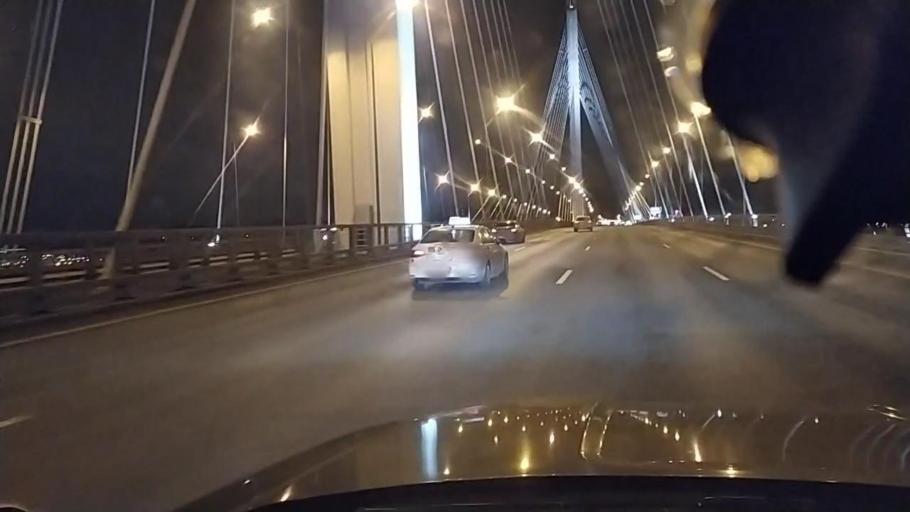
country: RU
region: St.-Petersburg
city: Staraya Derevnya
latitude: 59.9680
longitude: 30.2160
